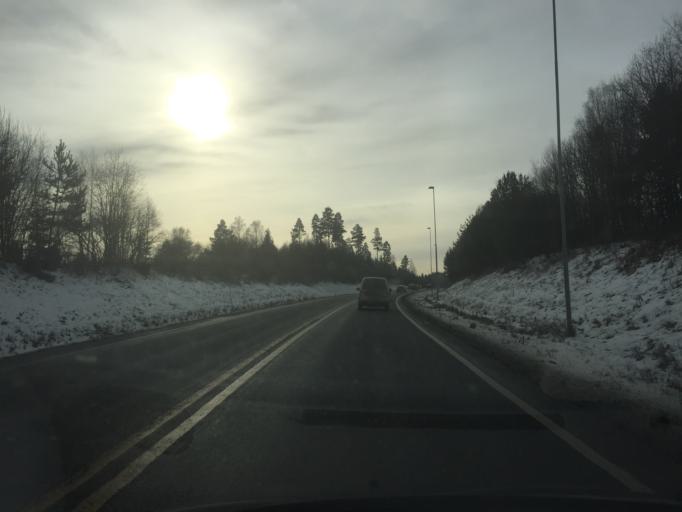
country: NO
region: Hedmark
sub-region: Loten
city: Loten
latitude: 60.7359
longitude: 11.2995
